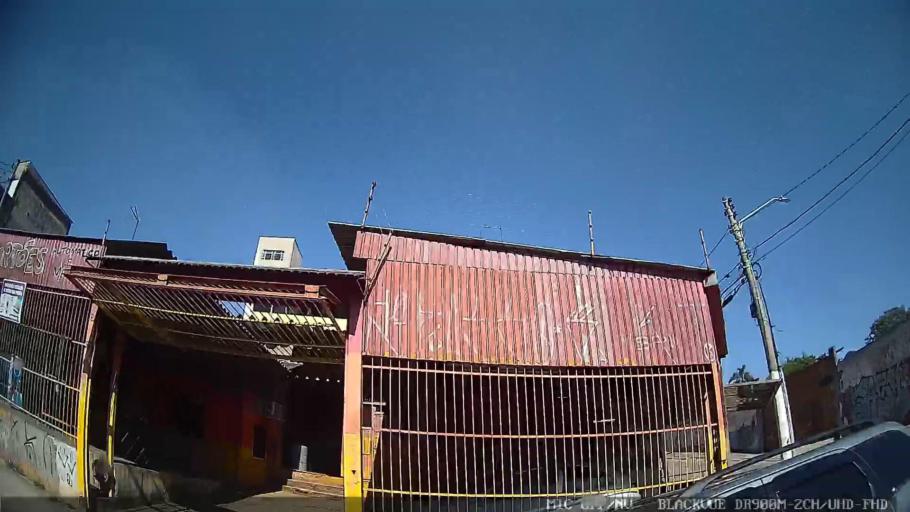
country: BR
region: Sao Paulo
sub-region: Ferraz De Vasconcelos
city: Ferraz de Vasconcelos
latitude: -23.5577
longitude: -46.4655
